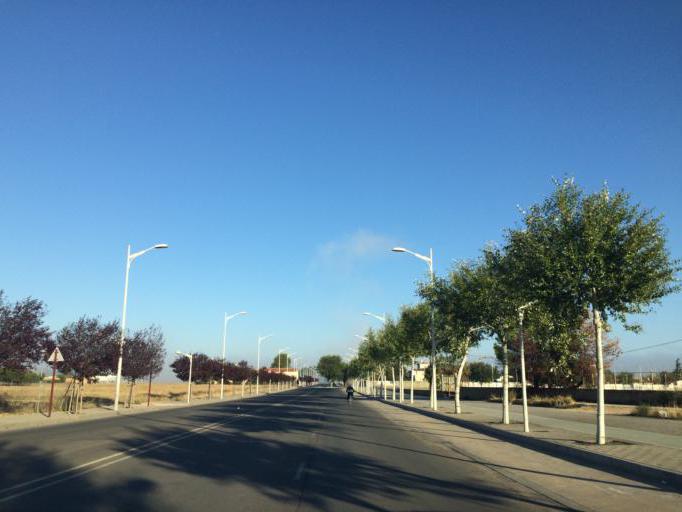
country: ES
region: Castille-La Mancha
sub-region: Provincia de Albacete
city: Albacete
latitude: 39.0012
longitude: -1.8779
